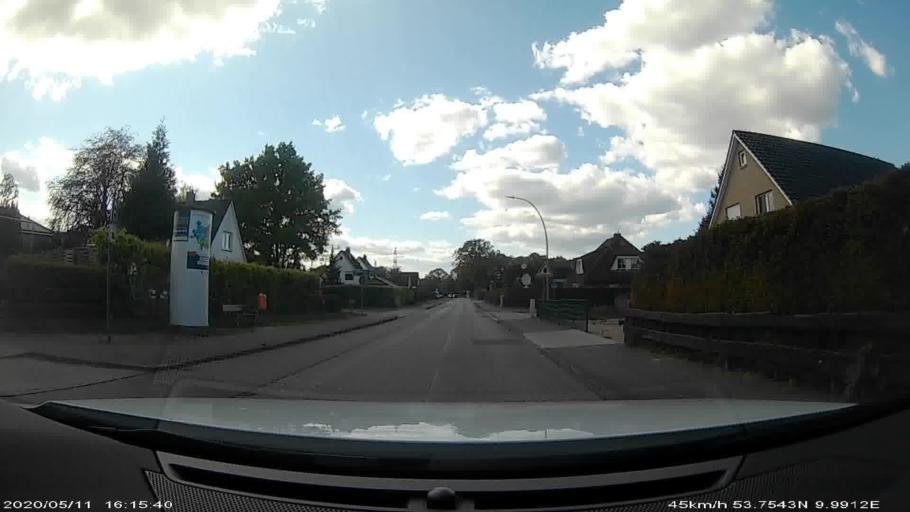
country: DE
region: Schleswig-Holstein
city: Henstedt-Ulzburg
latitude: 53.7551
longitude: 9.9826
